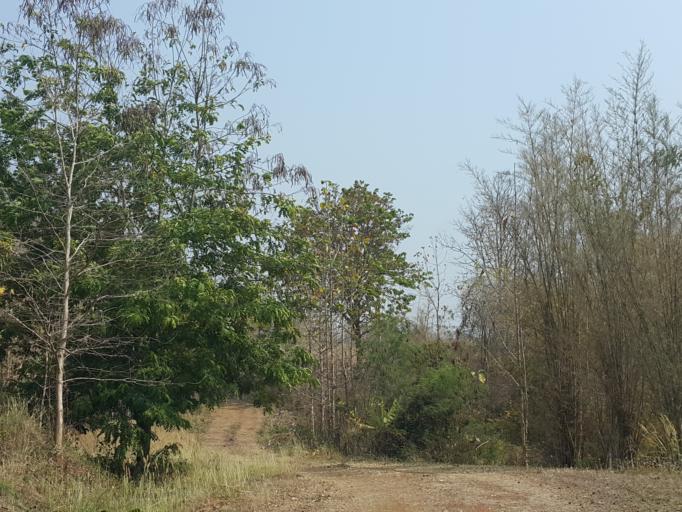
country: TH
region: Chiang Mai
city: Mae On
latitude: 18.7750
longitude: 99.2380
